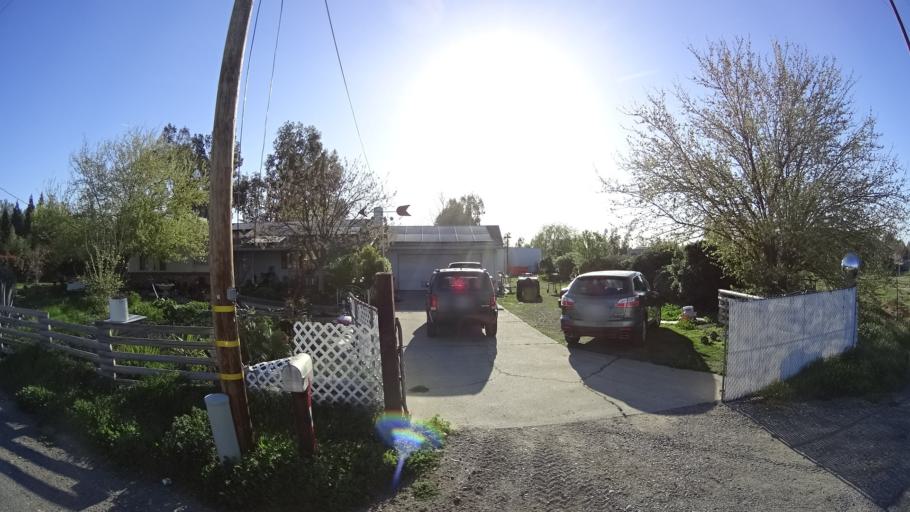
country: US
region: California
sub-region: Glenn County
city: Orland
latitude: 39.7603
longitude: -122.2156
